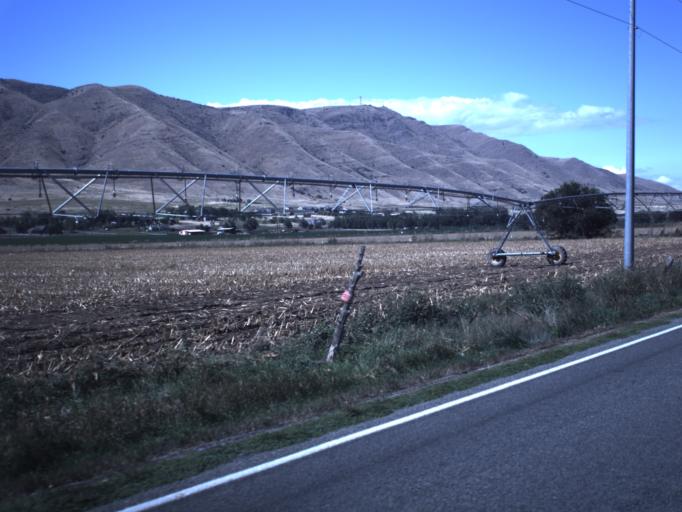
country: US
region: Utah
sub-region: Utah County
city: West Mountain
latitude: 40.0526
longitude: -111.7874
